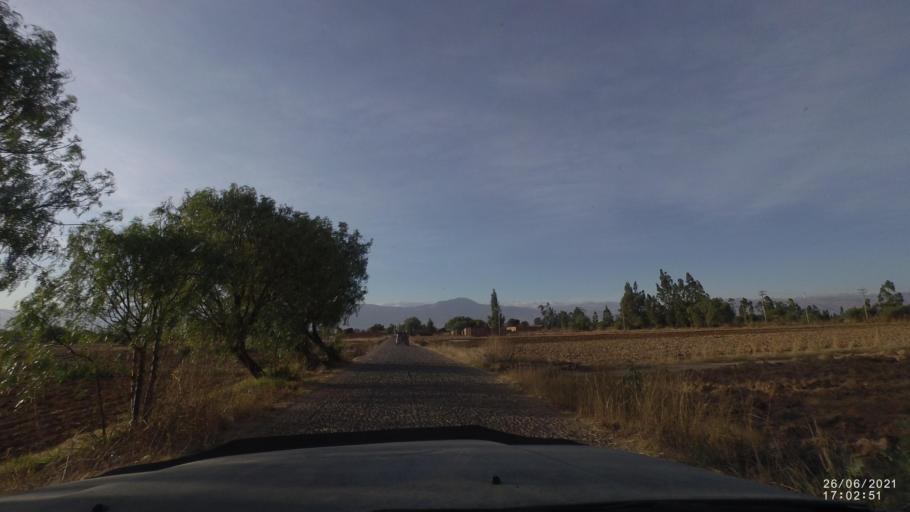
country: BO
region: Cochabamba
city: Cliza
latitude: -17.6496
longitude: -65.9126
